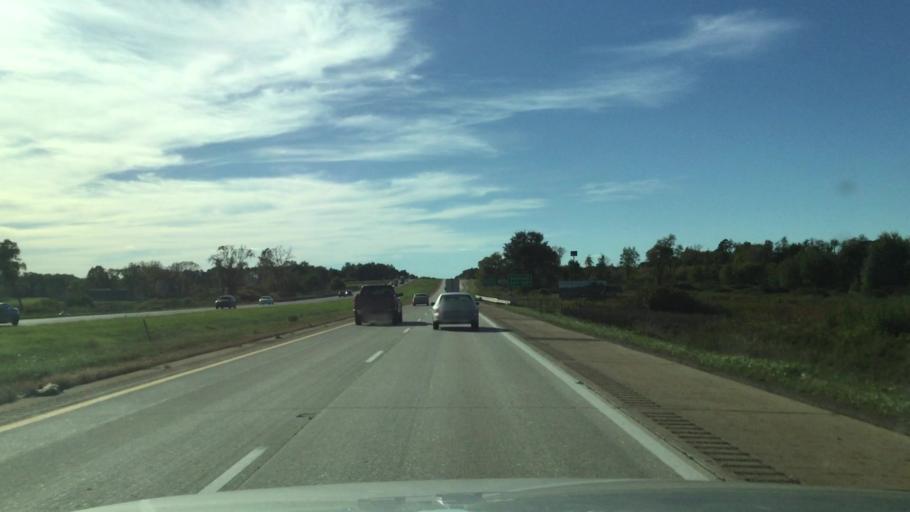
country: US
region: Michigan
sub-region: Jackson County
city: Concord
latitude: 42.2624
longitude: -84.6378
